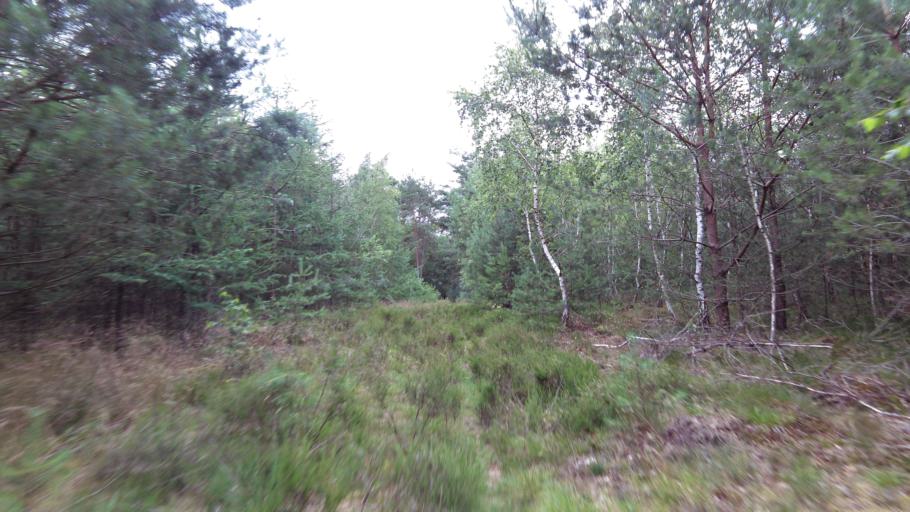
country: NL
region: Gelderland
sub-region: Gemeente Apeldoorn
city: Uddel
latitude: 52.2323
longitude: 5.7857
